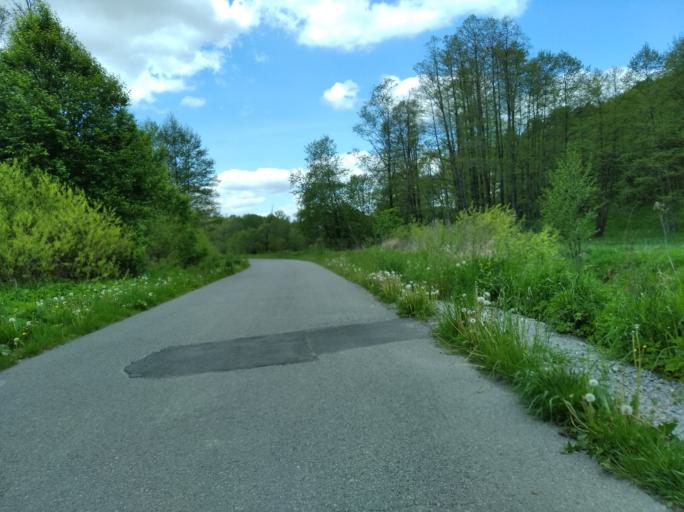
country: PL
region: Subcarpathian Voivodeship
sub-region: Powiat ropczycko-sedziszowski
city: Wielopole Skrzynskie
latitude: 49.9351
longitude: 21.6343
